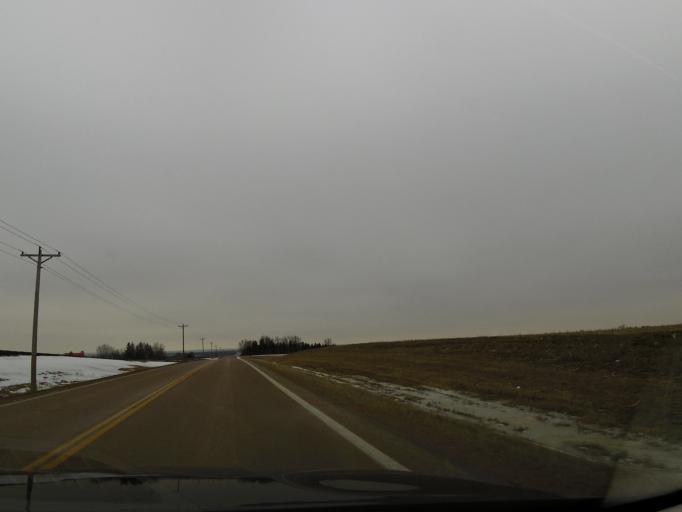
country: US
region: Minnesota
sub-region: Carver County
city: Carver
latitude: 44.7663
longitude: -93.6838
